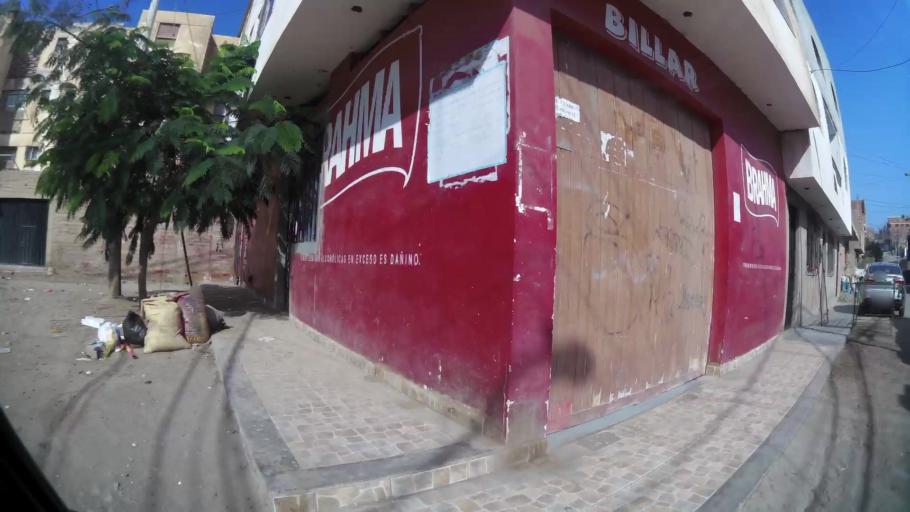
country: PE
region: Lima
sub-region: Huaura
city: Huacho
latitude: -11.1249
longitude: -77.6118
